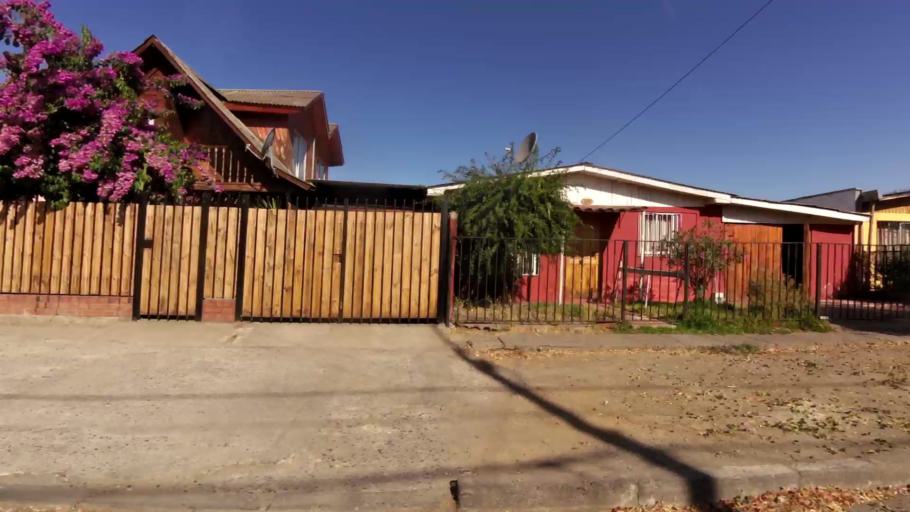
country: CL
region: Maule
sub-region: Provincia de Talca
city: Talca
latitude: -35.4459
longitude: -71.6566
